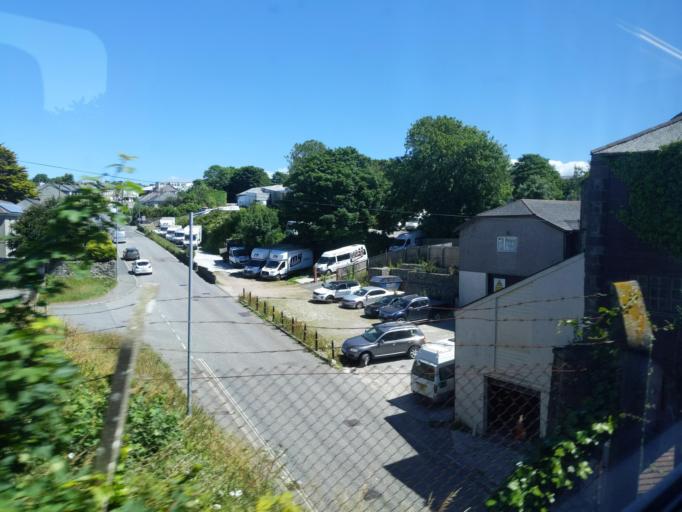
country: GB
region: England
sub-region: Cornwall
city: Redruth
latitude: 50.2375
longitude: -5.2253
